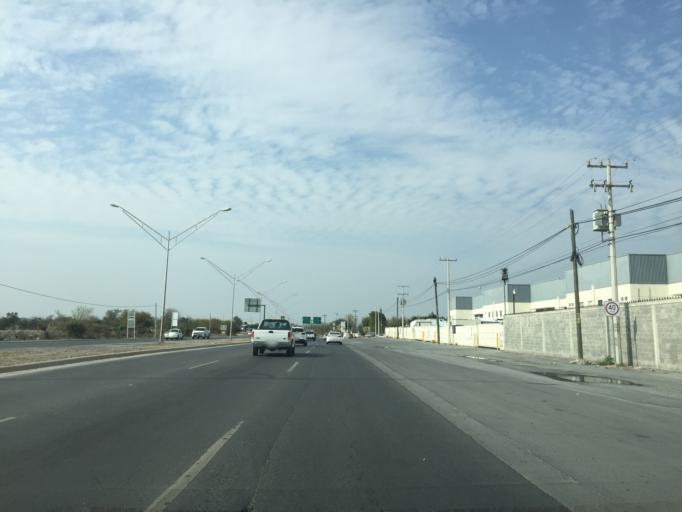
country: MX
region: Nuevo Leon
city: Apodaca
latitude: 25.7695
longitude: -100.1991
